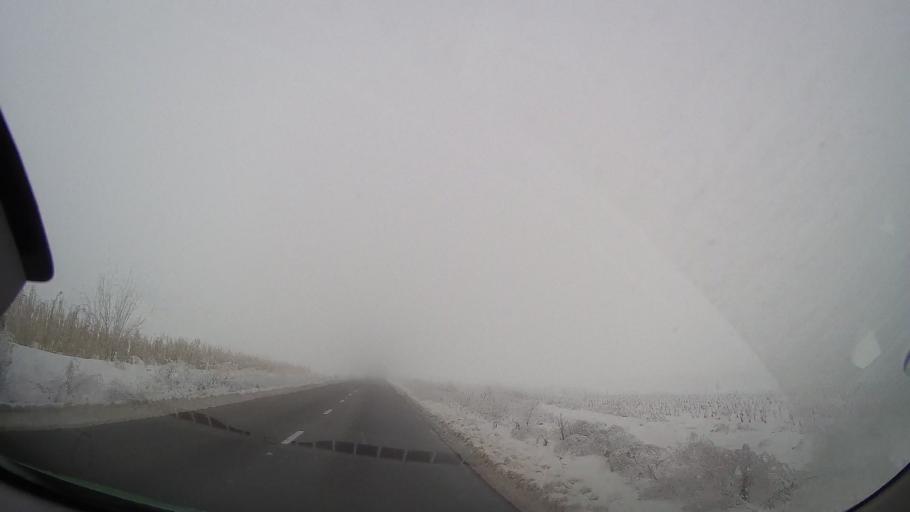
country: RO
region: Neamt
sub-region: Comuna Sabaoani
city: Sabaoani
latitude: 47.0351
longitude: 26.8549
